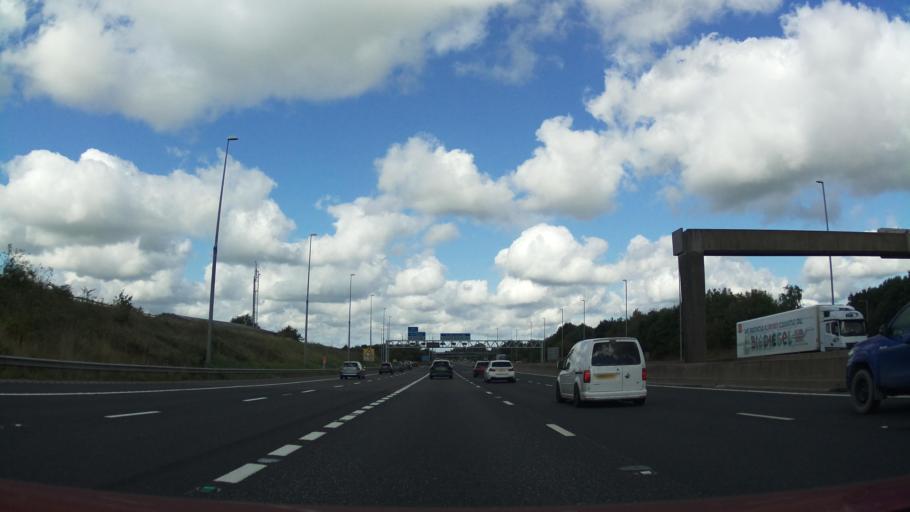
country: GB
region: England
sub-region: Lancashire
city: Goosnargh
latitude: 53.8015
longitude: -2.6879
